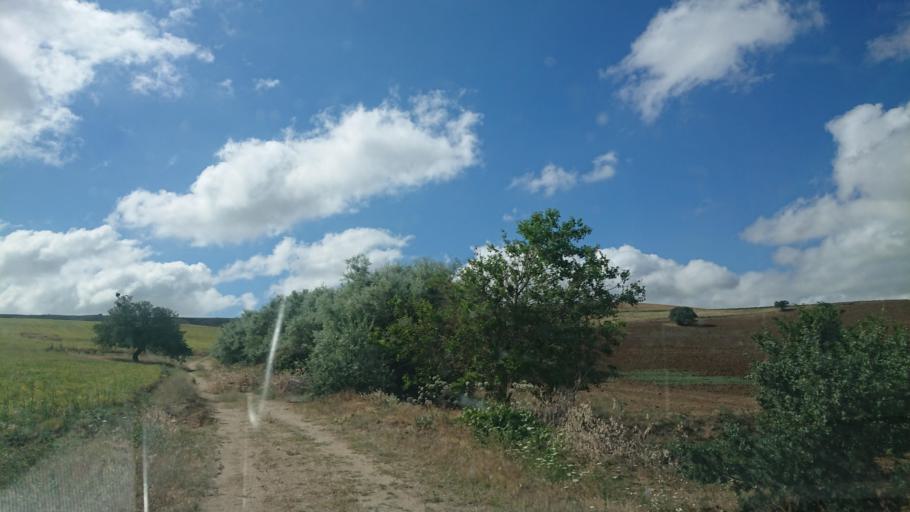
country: TR
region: Aksaray
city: Agacoren
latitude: 38.8432
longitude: 33.9367
